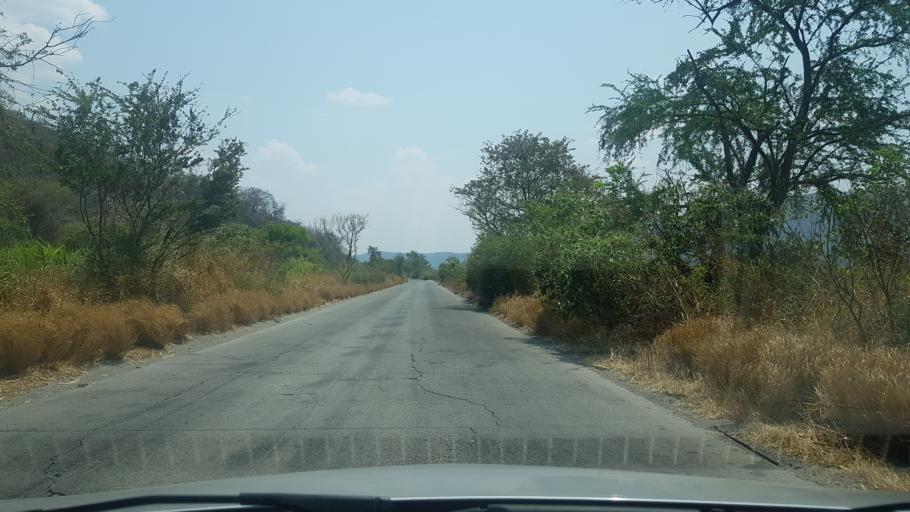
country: MX
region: Morelos
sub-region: Tlaltizapan de Zapata
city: Colonia Palo Prieto (Chipitongo)
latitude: 18.7754
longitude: -99.1070
